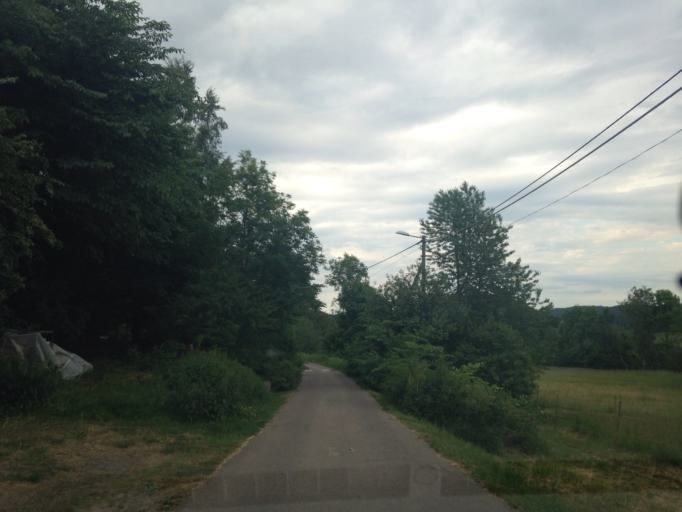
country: SE
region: Vaestra Goetaland
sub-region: Goteborg
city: Goeteborg
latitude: 57.7822
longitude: 11.9320
